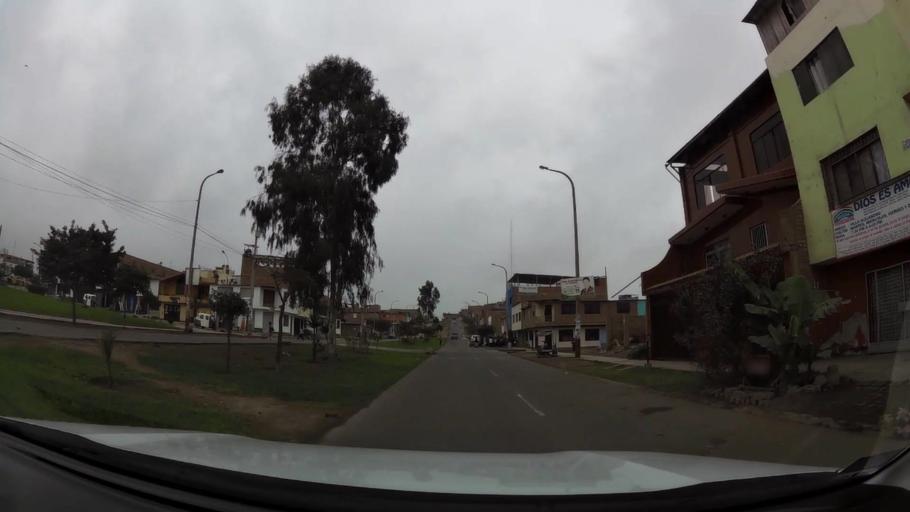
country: PE
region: Lima
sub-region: Lima
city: Punta Hermosa
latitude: -12.2381
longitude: -76.9110
